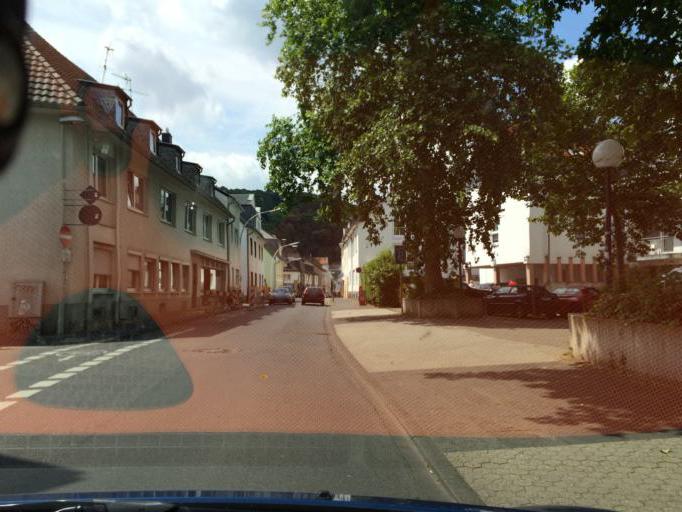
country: DE
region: North Rhine-Westphalia
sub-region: Regierungsbezirk Koln
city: Bonn
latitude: 50.7048
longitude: 7.1158
